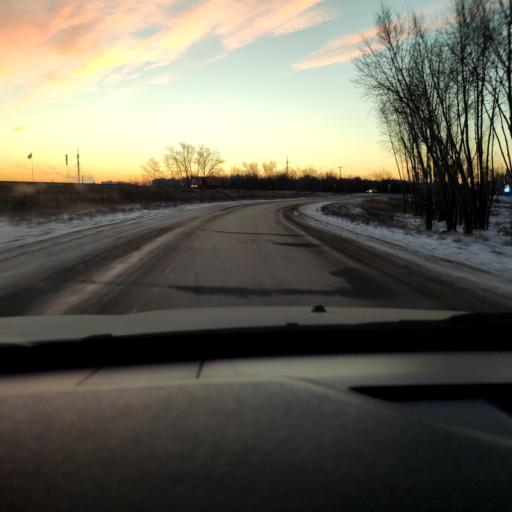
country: RU
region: Samara
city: Smyshlyayevka
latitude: 53.2579
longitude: 50.4740
